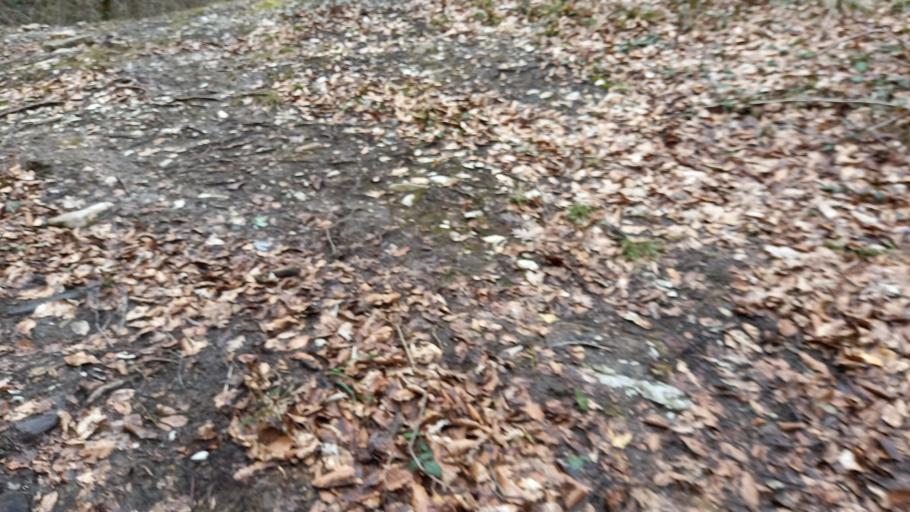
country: RU
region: Krasnodarskiy
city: Dzhubga
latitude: 44.3997
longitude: 38.7000
